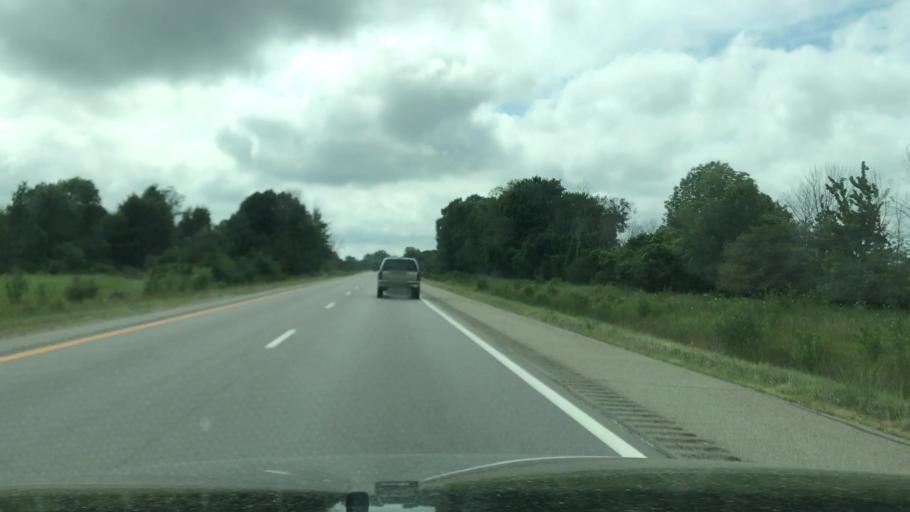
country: US
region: Michigan
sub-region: Ottawa County
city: Coopersville
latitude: 43.0705
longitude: -85.9993
